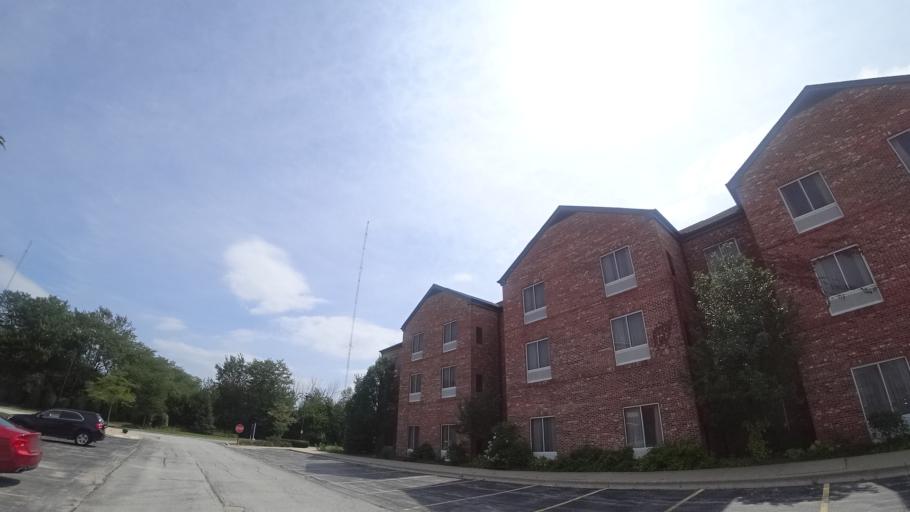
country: US
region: Illinois
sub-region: Cook County
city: Orland Hills
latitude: 41.5565
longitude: -87.8517
